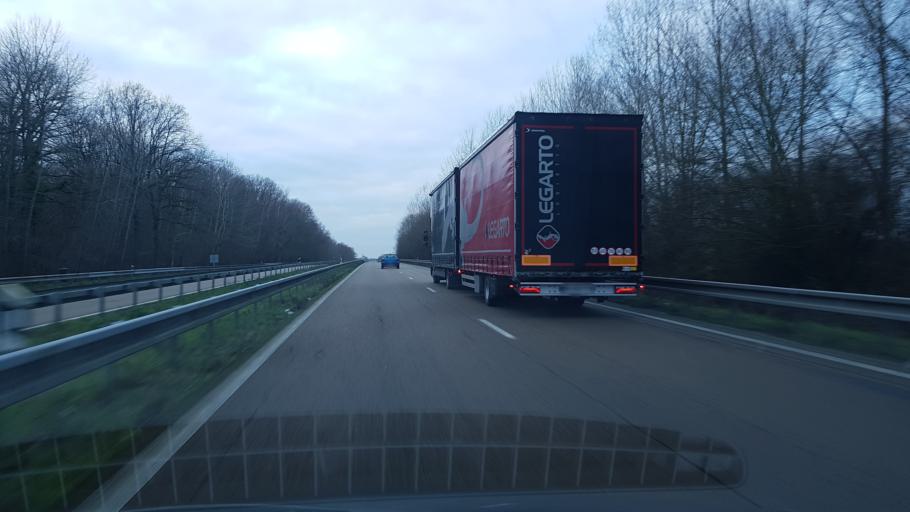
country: FR
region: Champagne-Ardenne
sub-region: Departement de la Marne
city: Esternay
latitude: 48.7302
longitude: 3.6424
